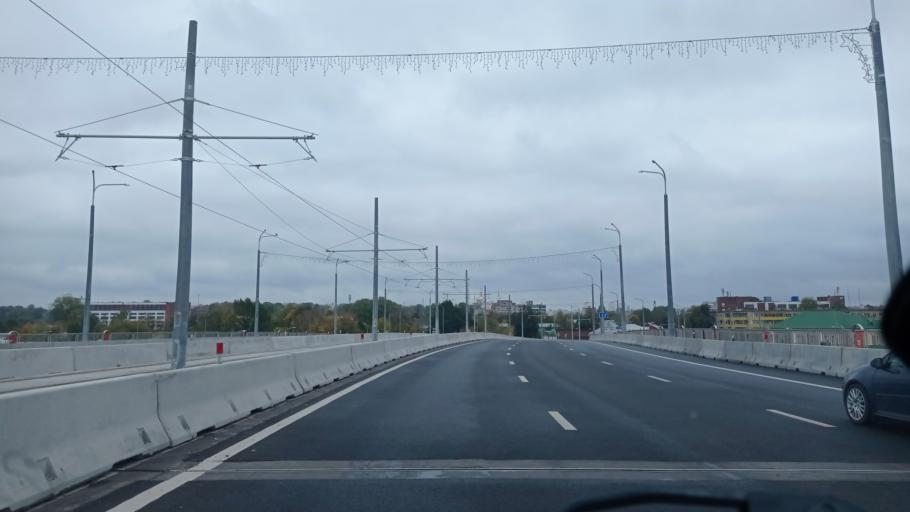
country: BY
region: Vitebsk
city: Vitebsk
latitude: 55.1987
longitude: 30.1856
